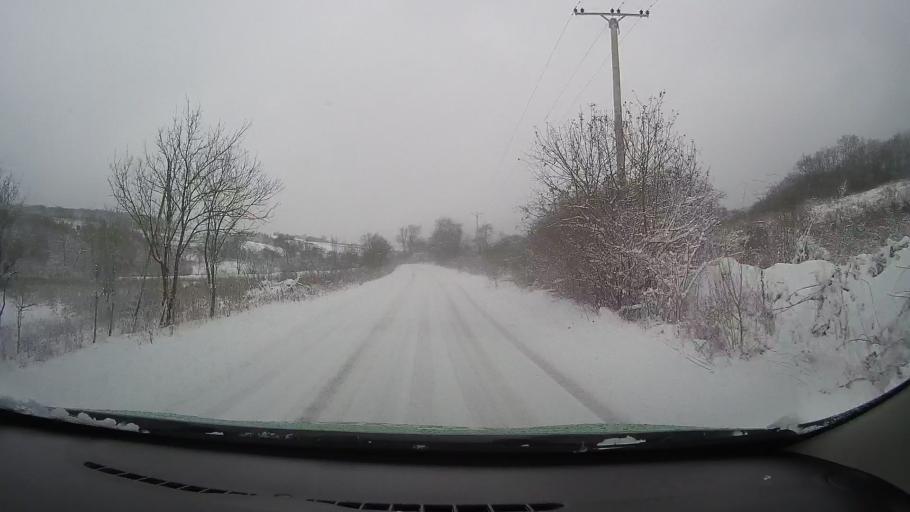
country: RO
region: Hunedoara
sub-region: Comuna Carjiti
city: Carjiti
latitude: 45.8359
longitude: 22.8385
